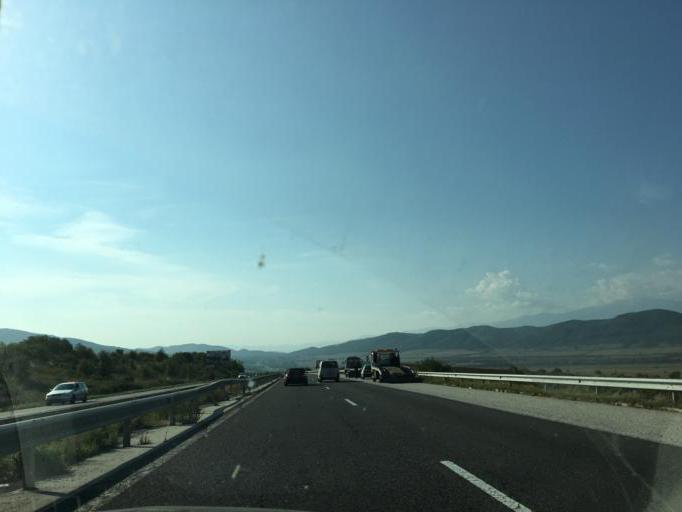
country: BG
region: Sofiya
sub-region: Obshtina Ikhtiman
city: Ikhtiman
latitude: 42.4283
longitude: 23.8537
